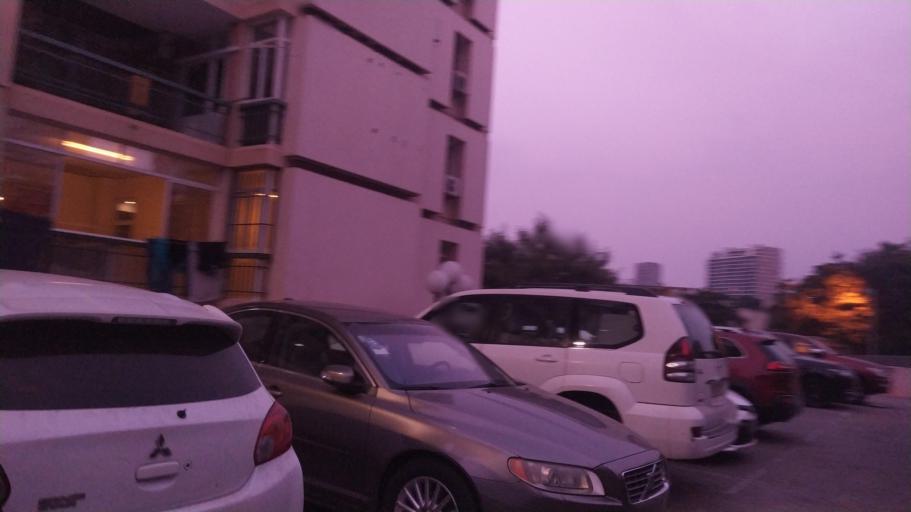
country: AO
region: Luanda
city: Luanda
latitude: -8.8341
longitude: 13.2319
